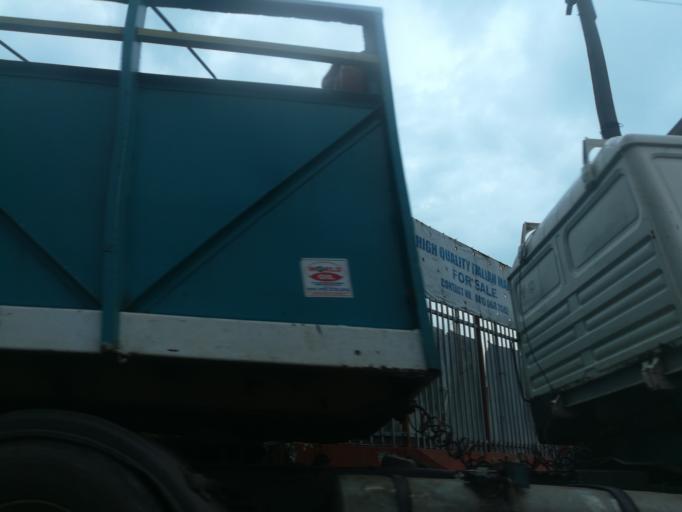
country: NG
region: Lagos
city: Agege
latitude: 6.6147
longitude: 3.3376
